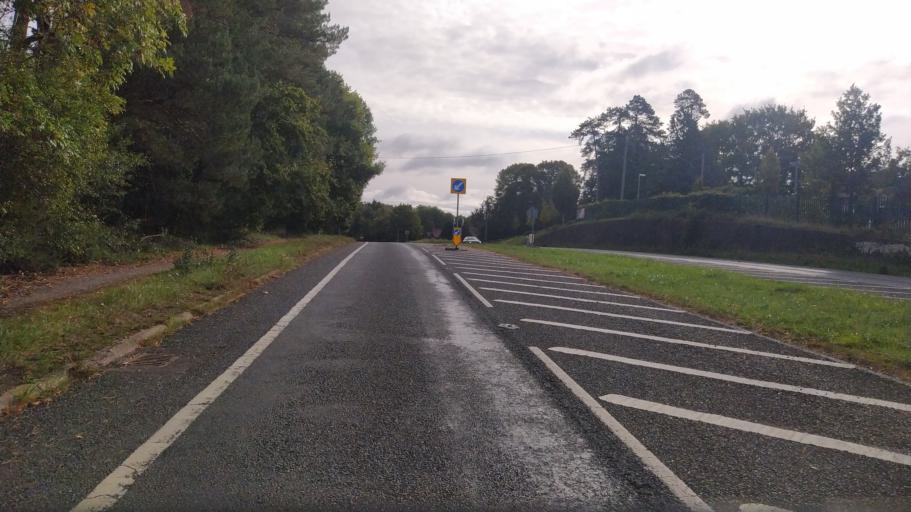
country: GB
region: England
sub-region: Hampshire
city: Hook
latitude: 51.2926
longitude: -0.9235
